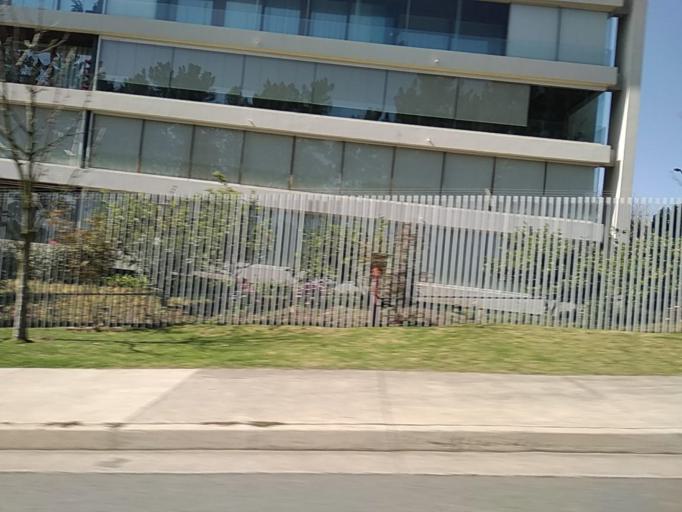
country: CL
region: Valparaiso
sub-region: Provincia de Valparaiso
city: Vina del Mar
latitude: -32.9433
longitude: -71.5375
